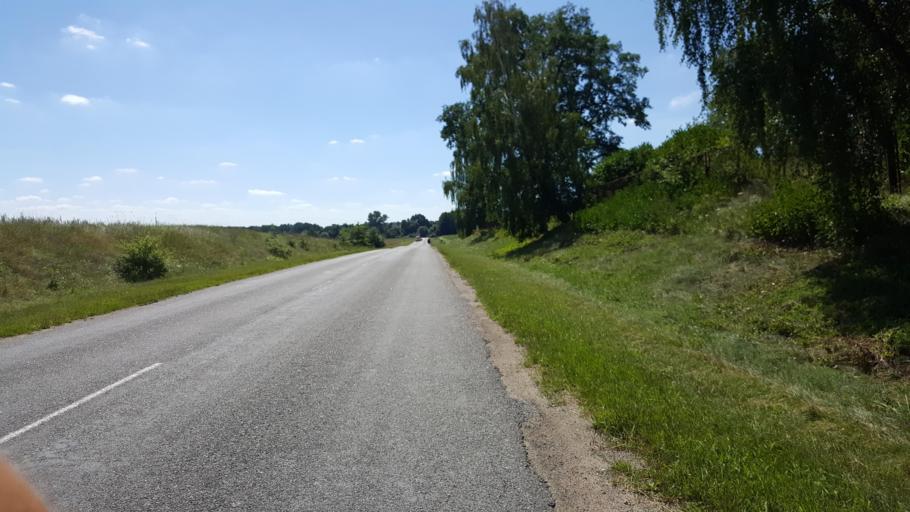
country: BY
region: Brest
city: Charnawchytsy
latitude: 52.3322
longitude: 23.6065
